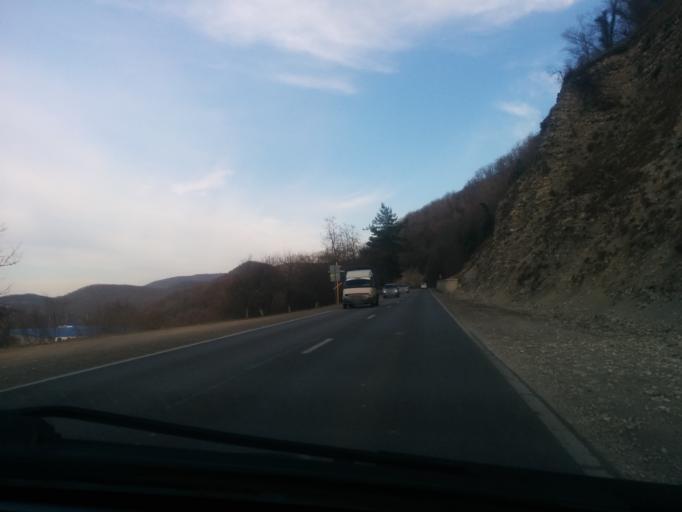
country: RU
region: Krasnodarskiy
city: Novomikhaylovskiy
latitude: 44.2559
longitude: 38.8698
